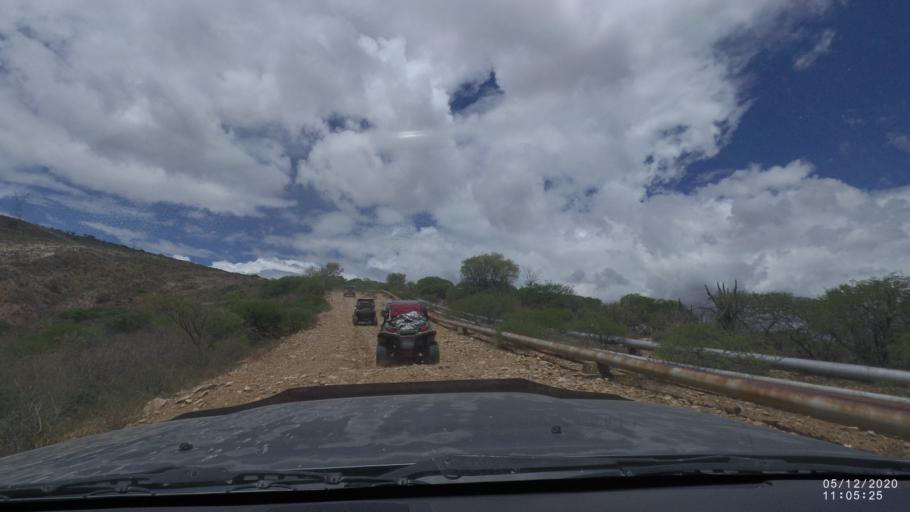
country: BO
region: Cochabamba
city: Sipe Sipe
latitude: -17.5495
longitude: -66.3035
